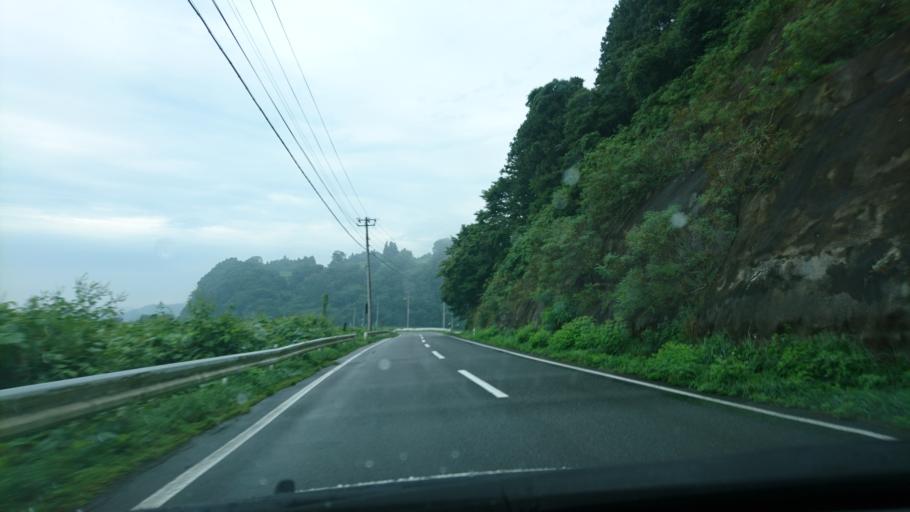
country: JP
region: Iwate
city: Ichinoseki
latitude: 38.8866
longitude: 141.2657
